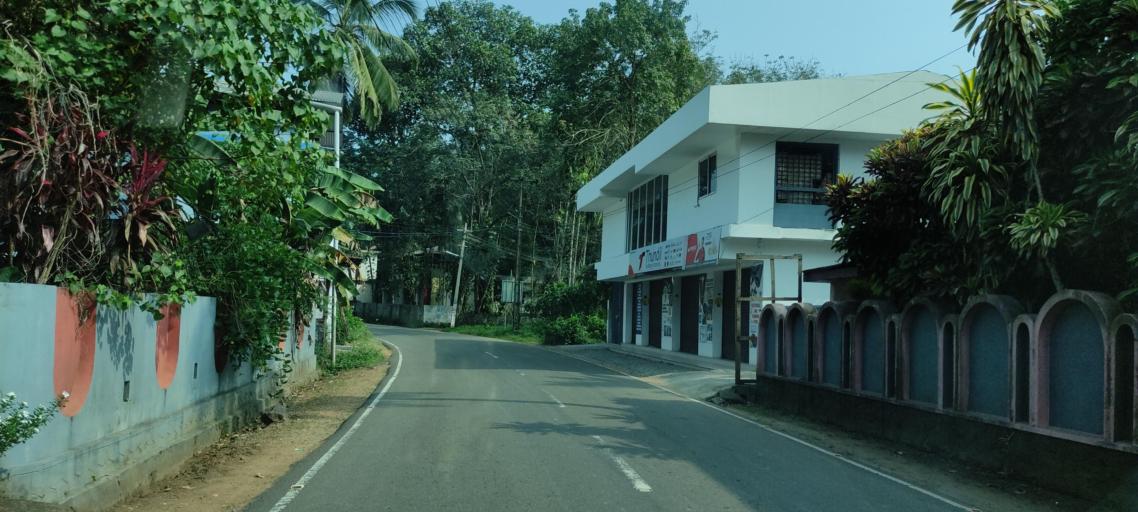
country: IN
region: Kerala
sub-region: Pattanamtitta
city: Pathanamthitta
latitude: 9.2313
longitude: 76.7487
